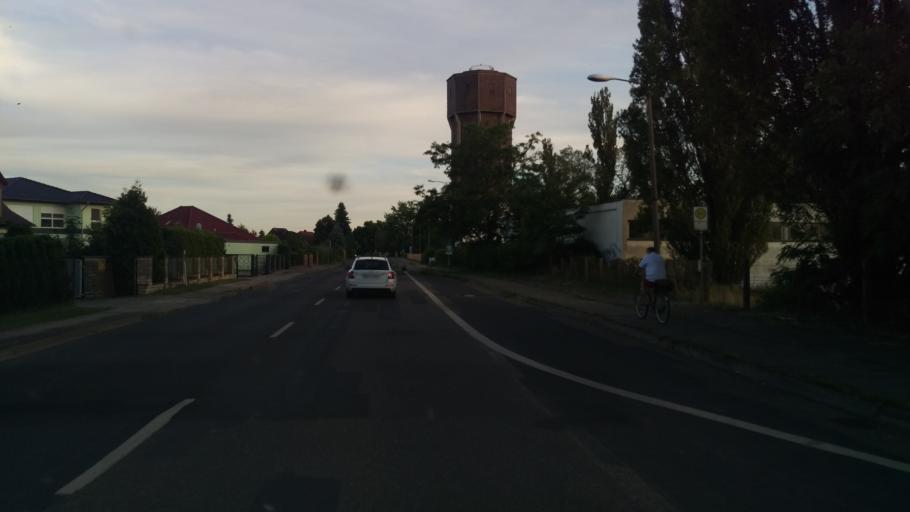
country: DE
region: Brandenburg
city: Eisenhuettenstadt
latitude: 52.1522
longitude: 14.6733
